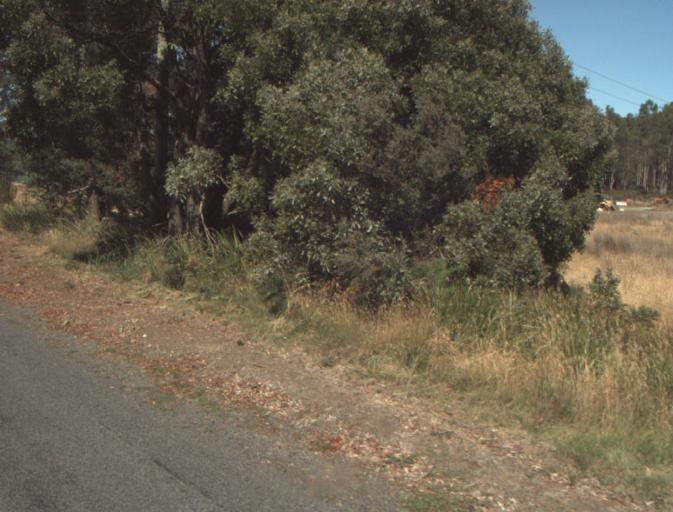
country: AU
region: Tasmania
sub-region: Launceston
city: Newstead
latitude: -41.3737
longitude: 147.2973
